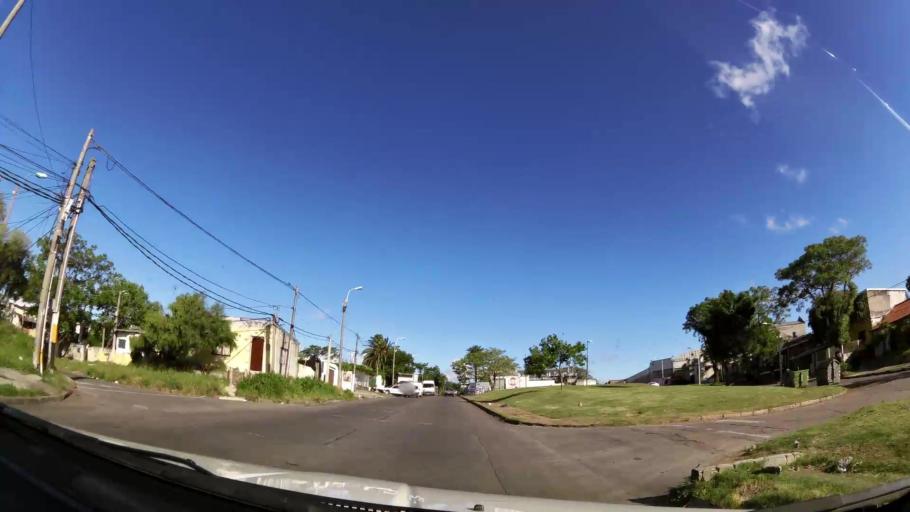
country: UY
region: Montevideo
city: Montevideo
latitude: -34.8530
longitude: -56.2378
